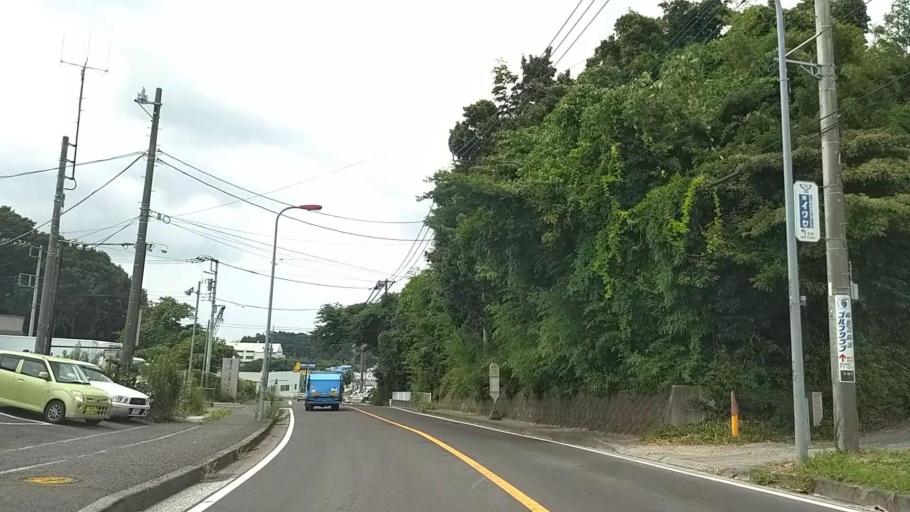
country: JP
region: Kanagawa
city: Minami-rinkan
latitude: 35.4395
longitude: 139.4471
